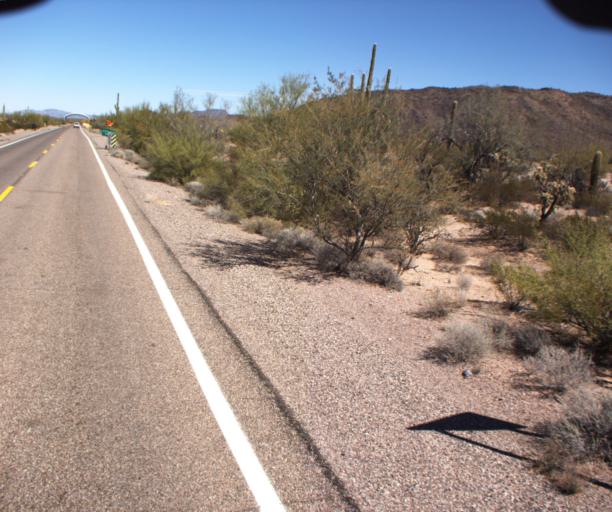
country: US
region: Arizona
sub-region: Pima County
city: Ajo
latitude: 32.1980
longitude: -112.7597
